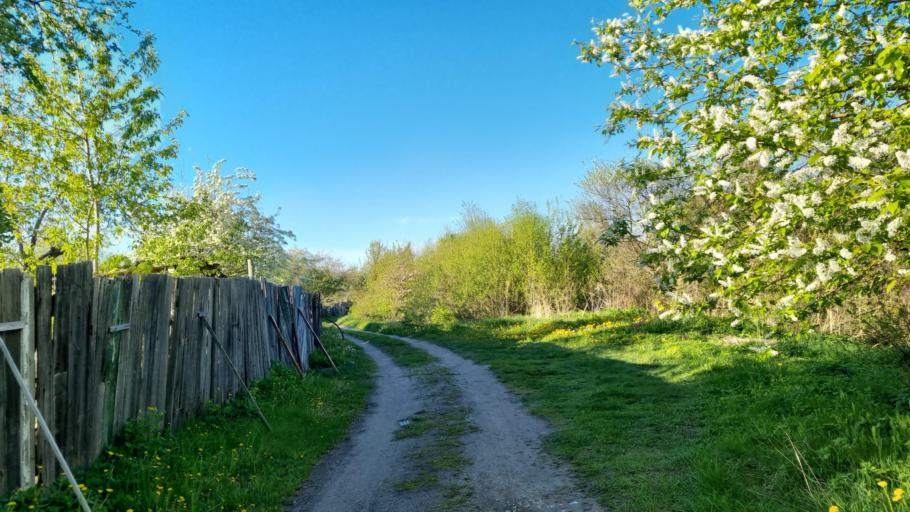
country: LV
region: Riga
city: Bolderaja
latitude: 56.9917
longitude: 24.0582
